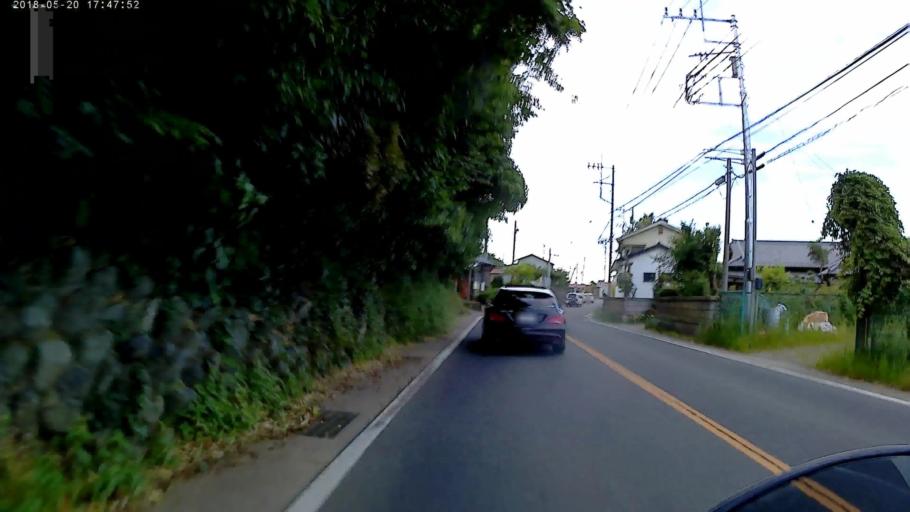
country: JP
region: Kanagawa
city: Oiso
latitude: 35.3366
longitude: 139.2928
